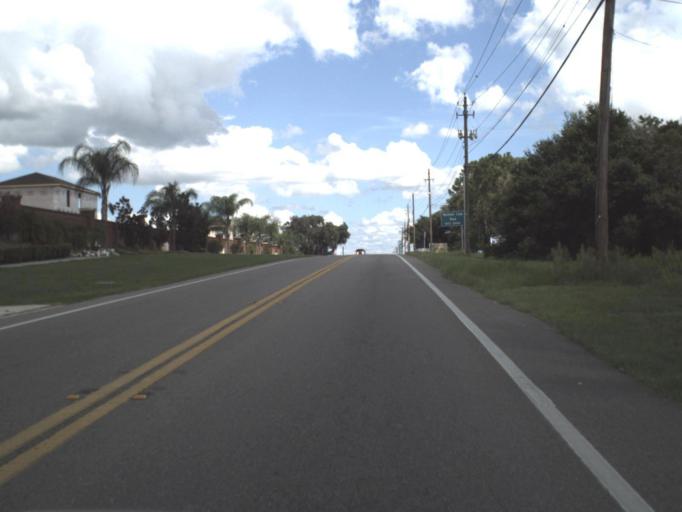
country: US
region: Florida
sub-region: Polk County
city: Cypress Gardens
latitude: 28.0225
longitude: -81.6982
